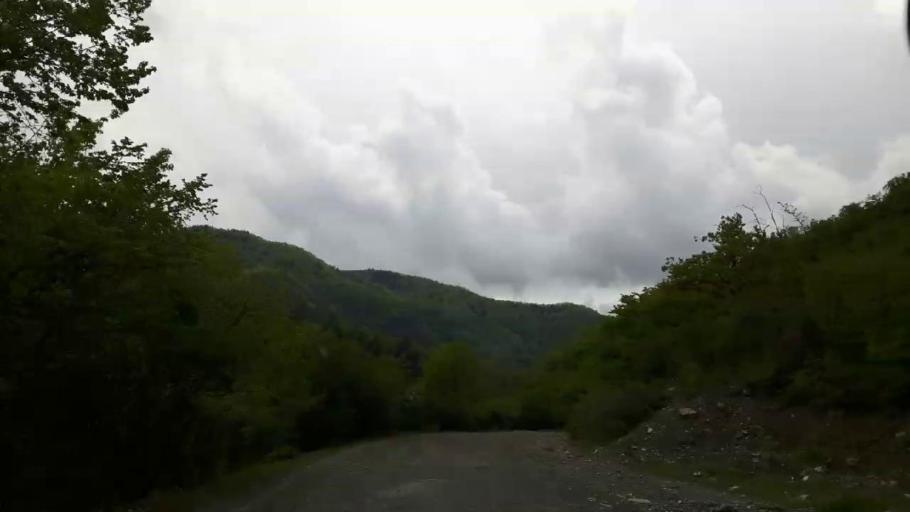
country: GE
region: Shida Kartli
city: Gori
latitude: 41.8711
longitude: 43.9855
